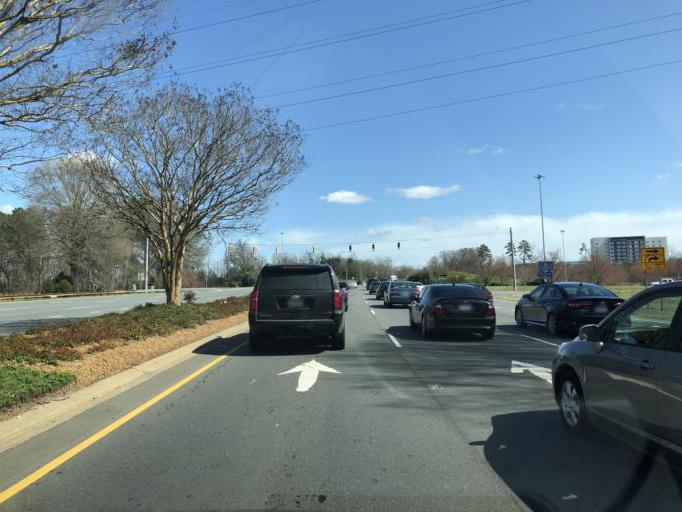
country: US
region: North Carolina
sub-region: Cabarrus County
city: Harrisburg
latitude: 35.3130
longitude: -80.7609
